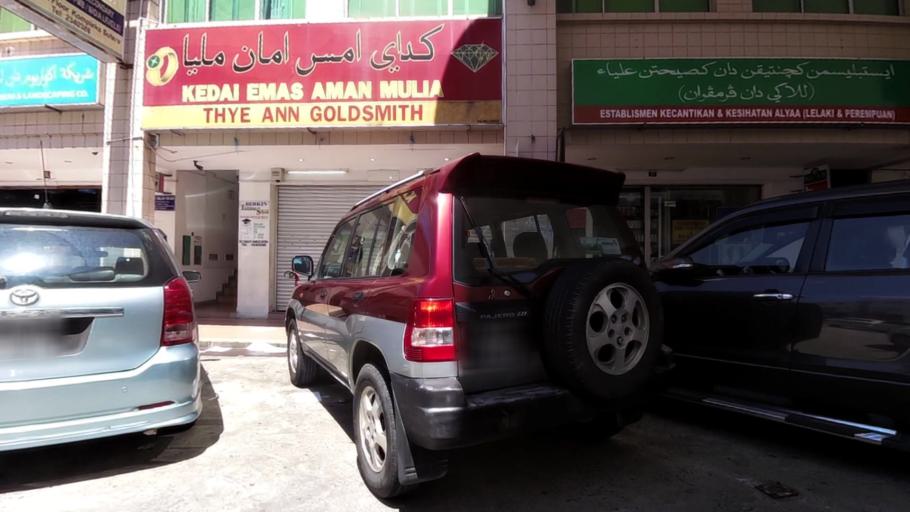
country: BN
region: Brunei and Muara
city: Bandar Seri Begawan
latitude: 4.9438
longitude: 114.9464
